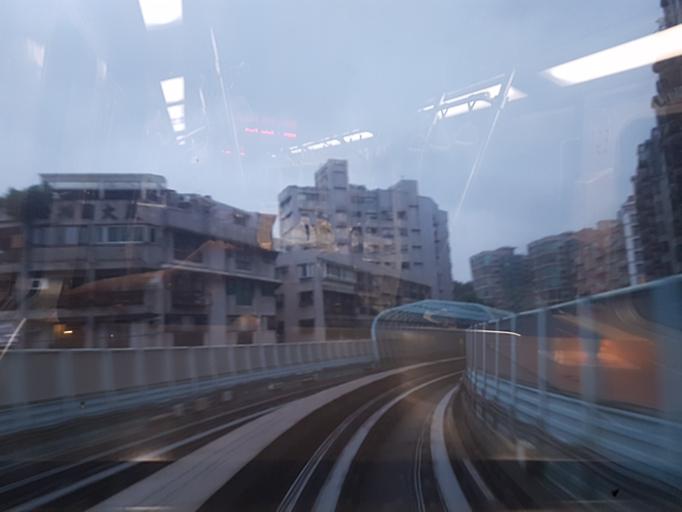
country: TW
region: Taipei
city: Taipei
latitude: 25.0735
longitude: 121.6061
